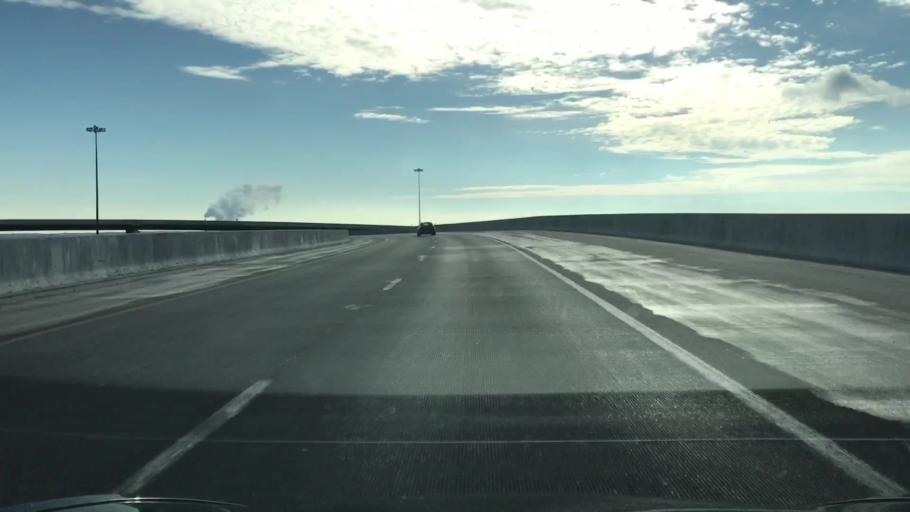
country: US
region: Nebraska
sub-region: Douglas County
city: Omaha
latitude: 41.2343
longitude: -95.8991
